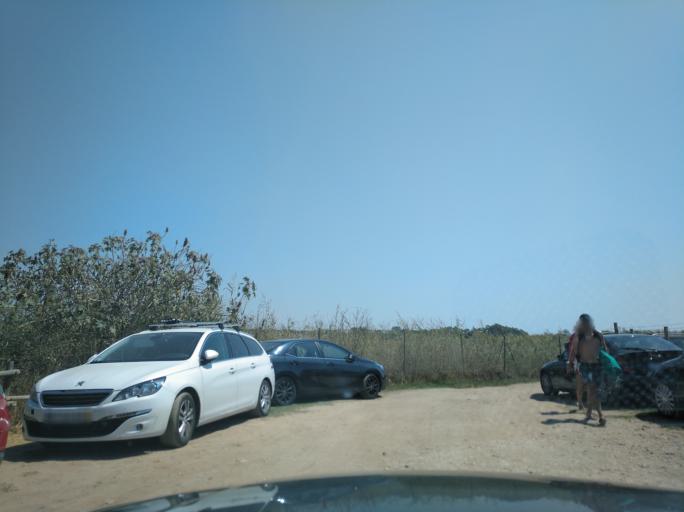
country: PT
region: Faro
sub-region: Vila Real de Santo Antonio
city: Monte Gordo
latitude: 37.1745
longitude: -7.4934
